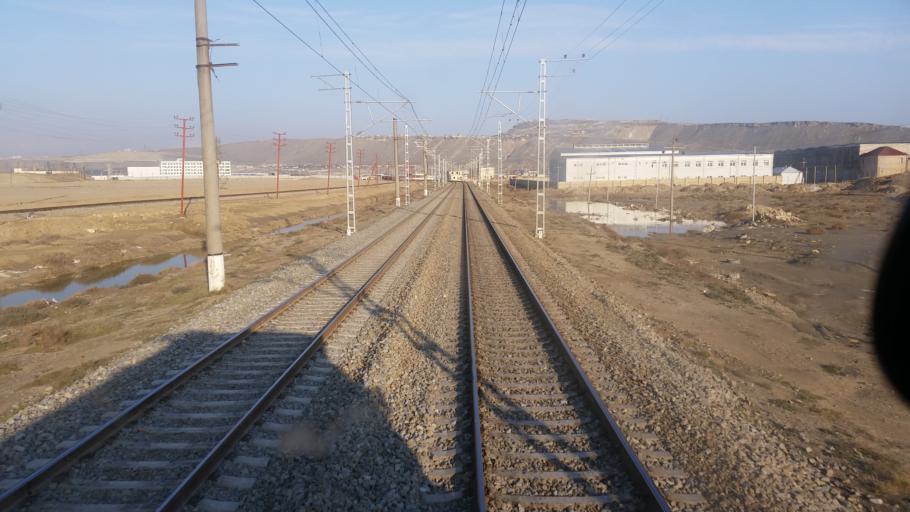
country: AZ
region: Baki
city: Lokbatan
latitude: 40.3226
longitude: 49.7554
